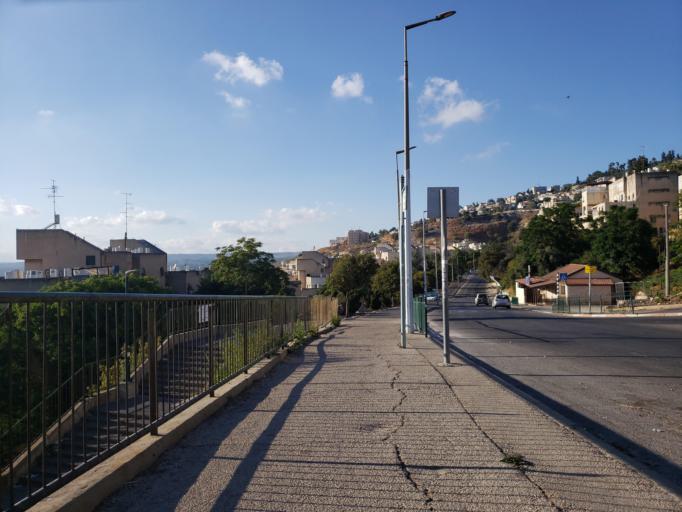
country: IL
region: Northern District
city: Safed
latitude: 32.9597
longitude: 35.4915
